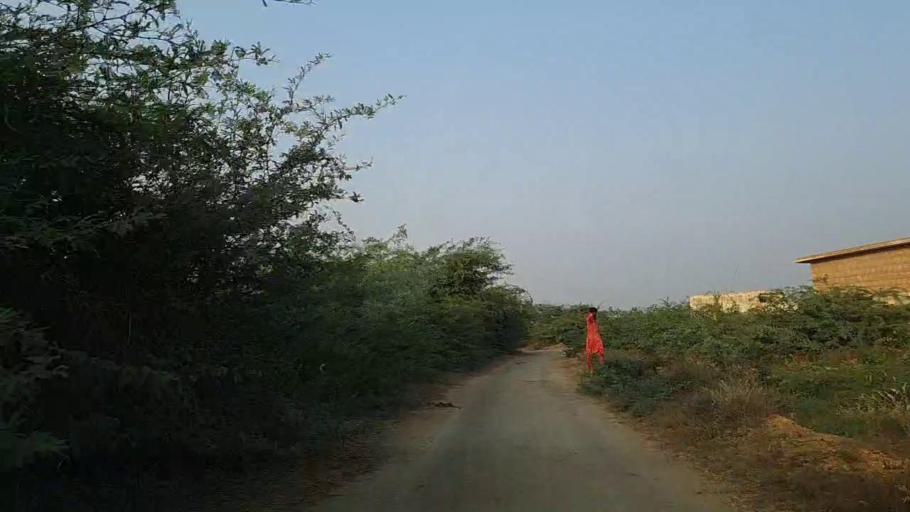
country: PK
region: Sindh
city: Thatta
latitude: 24.6902
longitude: 67.8205
